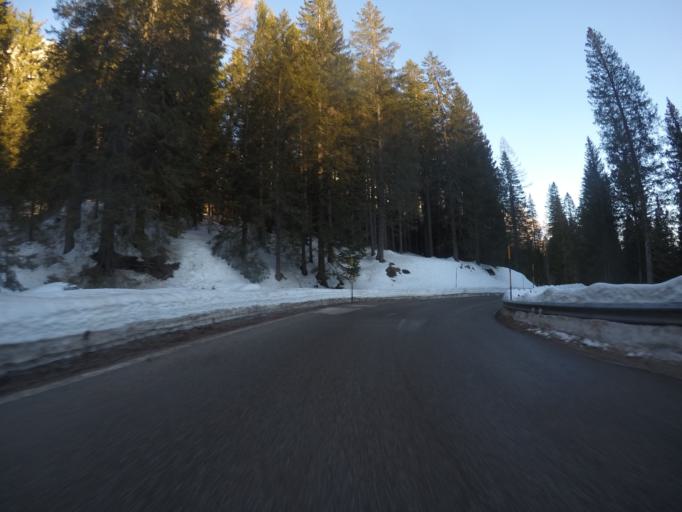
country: IT
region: Trentino-Alto Adige
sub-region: Provincia di Trento
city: Siror
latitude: 46.2723
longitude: 11.8008
